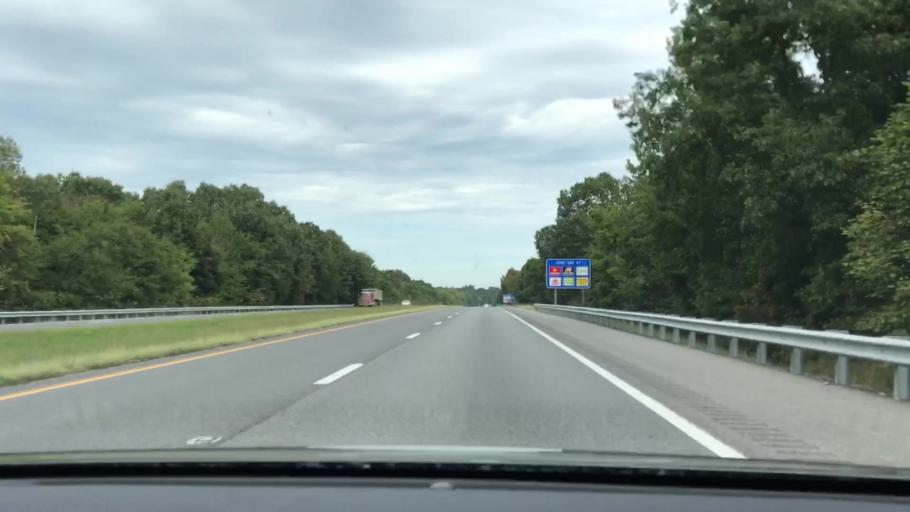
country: US
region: Kentucky
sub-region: Marshall County
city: Benton
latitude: 36.9082
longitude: -88.3486
